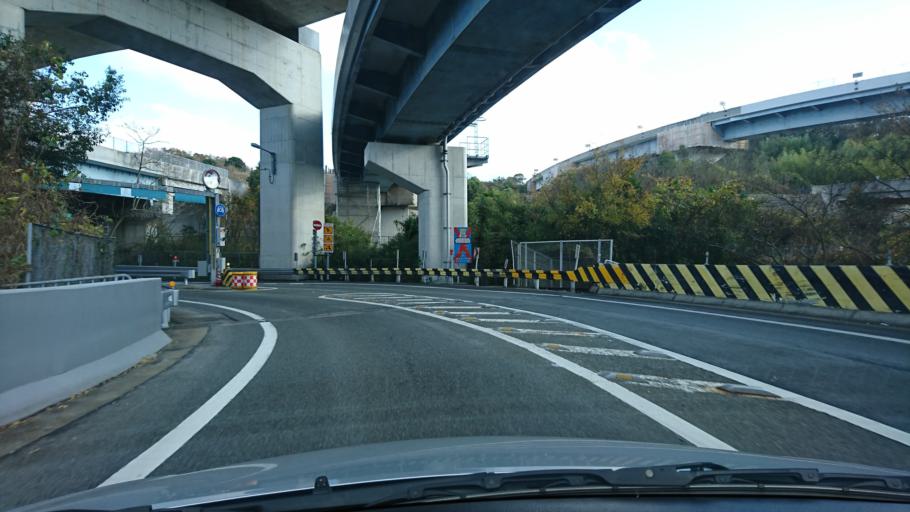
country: JP
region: Hyogo
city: Akashi
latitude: 34.6852
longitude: 135.0225
